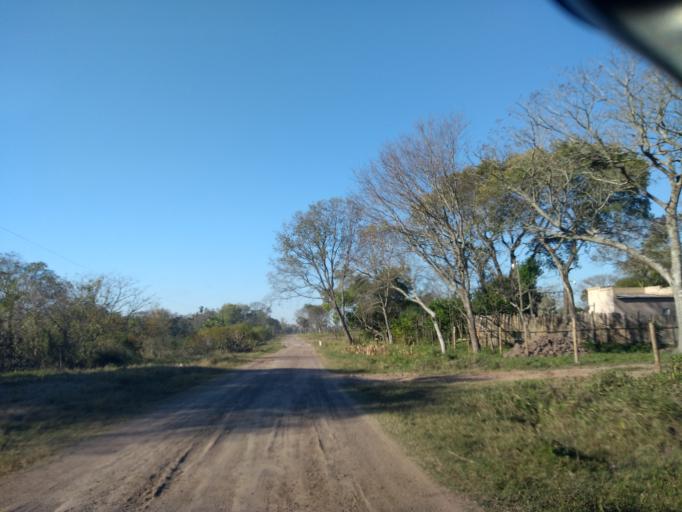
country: AR
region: Chaco
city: Barranqueras
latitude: -27.4378
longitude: -58.9289
